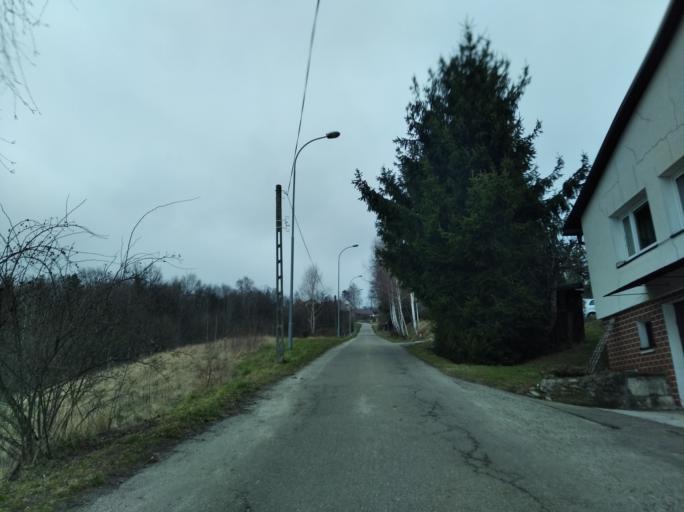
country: PL
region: Subcarpathian Voivodeship
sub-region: Powiat strzyzowski
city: Strzyzow
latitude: 49.8764
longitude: 21.8046
